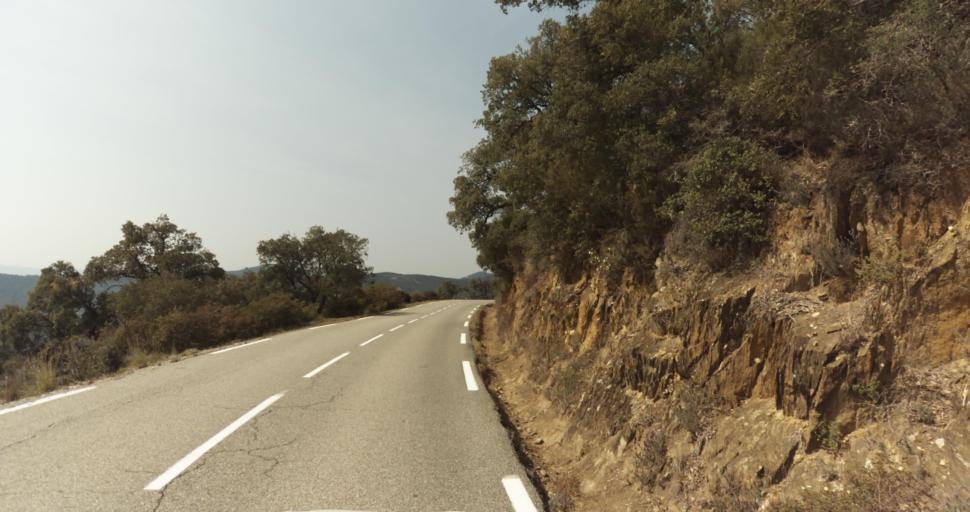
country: FR
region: Provence-Alpes-Cote d'Azur
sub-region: Departement du Var
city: Bormes-les-Mimosas
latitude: 43.1628
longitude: 6.3347
